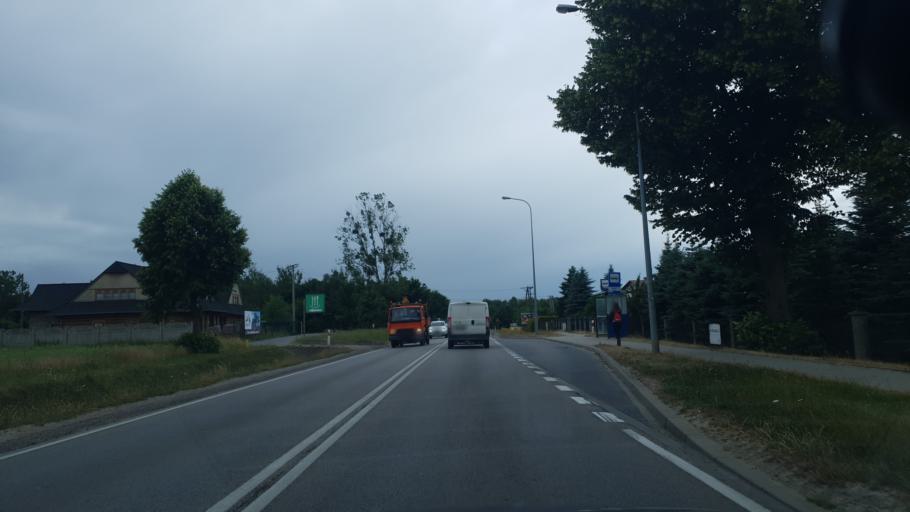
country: PL
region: Pomeranian Voivodeship
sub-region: Powiat kartuski
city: Banino
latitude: 54.4028
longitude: 18.3618
